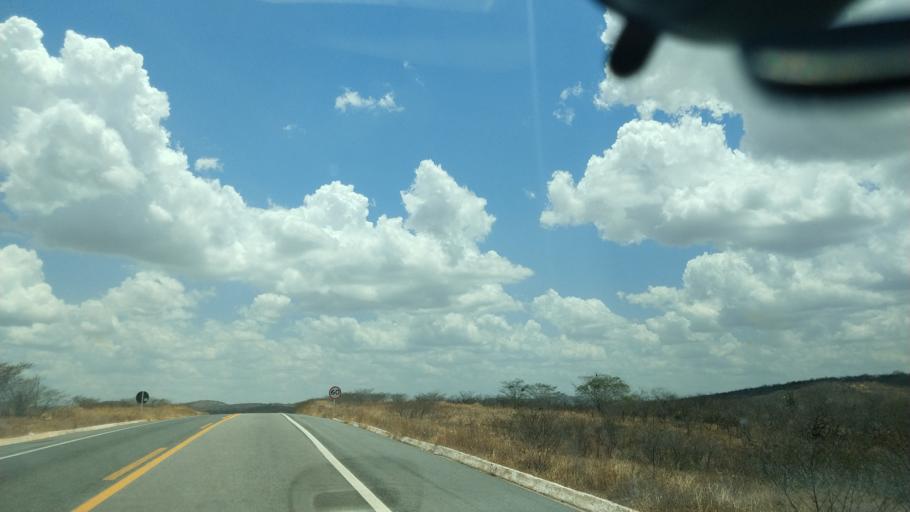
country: BR
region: Rio Grande do Norte
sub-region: Currais Novos
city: Currais Novos
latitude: -6.2488
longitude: -36.4724
